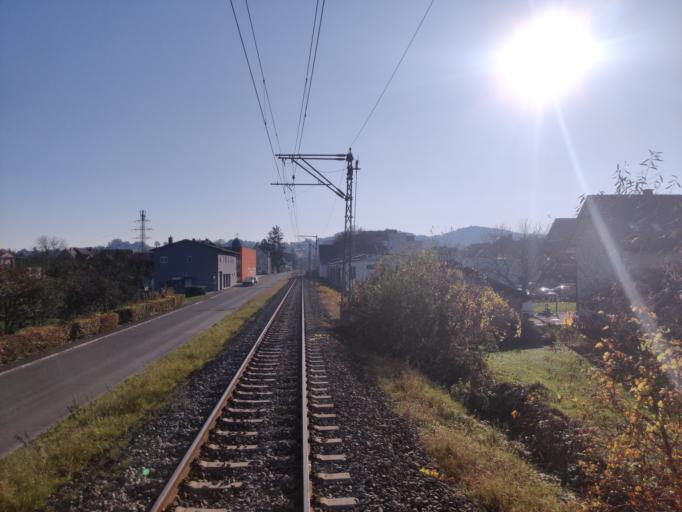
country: AT
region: Styria
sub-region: Politischer Bezirk Suedoststeiermark
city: Feldbach
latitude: 46.9530
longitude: 15.8980
